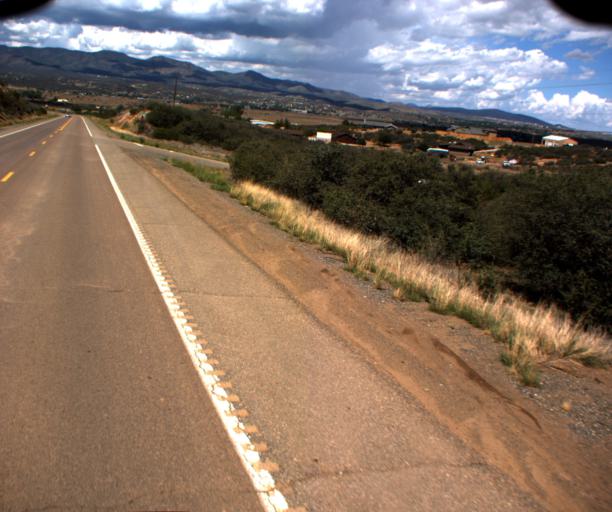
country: US
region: Arizona
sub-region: Yavapai County
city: Dewey-Humboldt
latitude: 34.5391
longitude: -112.2026
